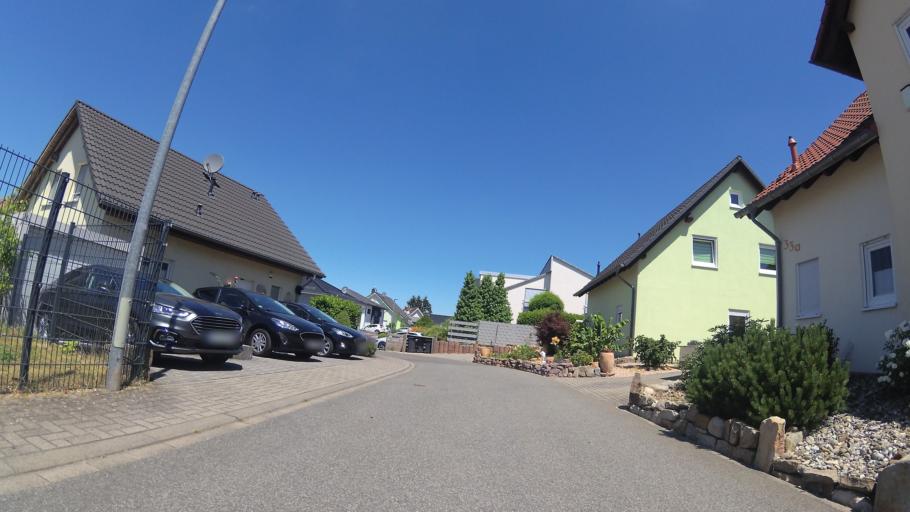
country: DE
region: Saarland
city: Neunkirchen
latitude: 49.3588
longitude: 7.1821
